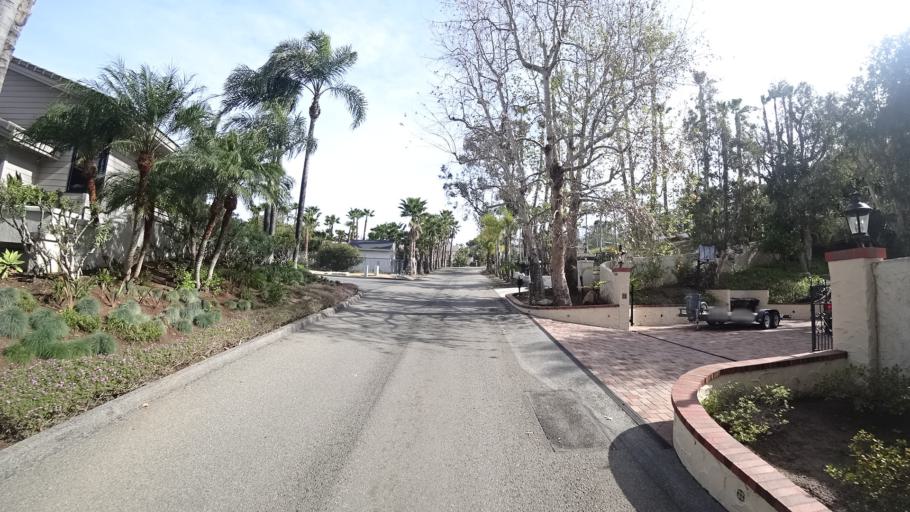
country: US
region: California
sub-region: Orange County
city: Yorba Linda
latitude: 33.8562
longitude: -117.7637
